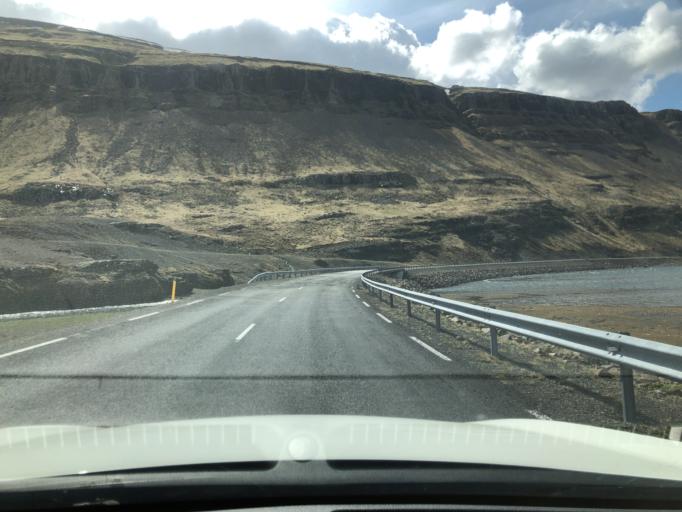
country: IS
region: Capital Region
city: Mosfellsbaer
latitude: 64.3835
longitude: -21.3547
